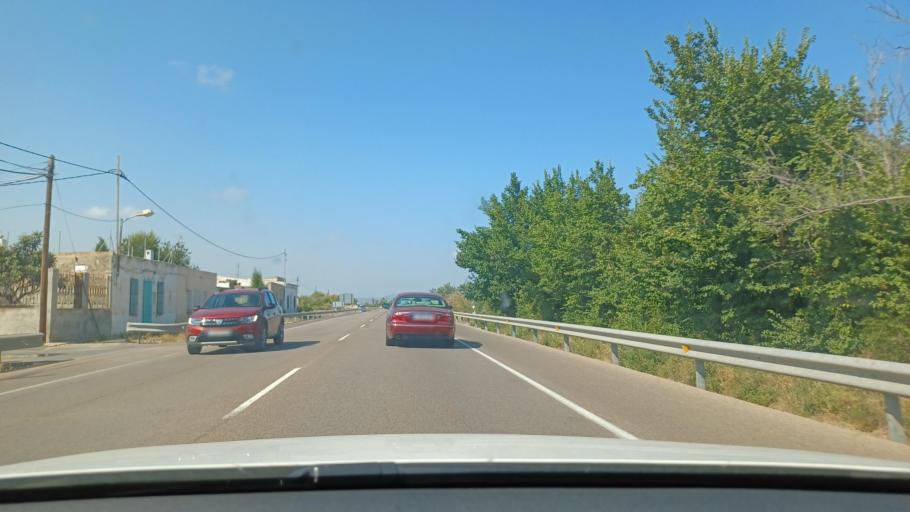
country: ES
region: Valencia
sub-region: Provincia de Castello
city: Orpesa/Oropesa del Mar
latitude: 40.1557
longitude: 0.1602
